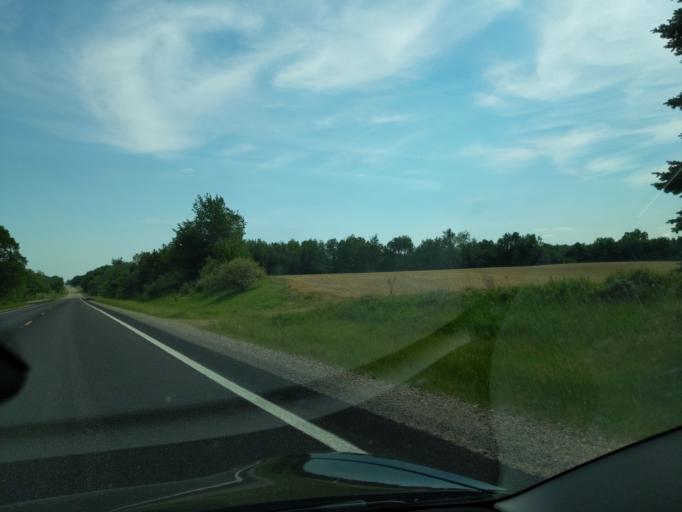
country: US
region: Michigan
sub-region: Barry County
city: Nashville
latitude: 42.6861
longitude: -85.0953
